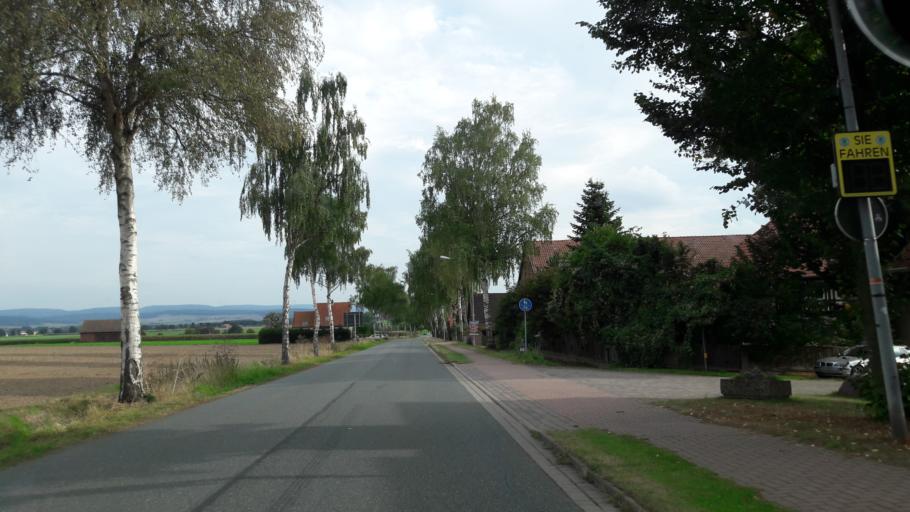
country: DE
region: Lower Saxony
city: Bockenem
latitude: 52.0373
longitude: 10.0856
